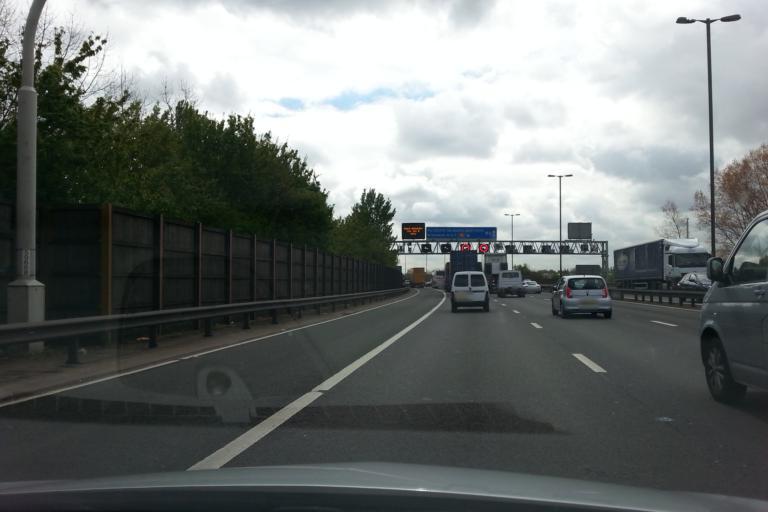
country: GB
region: England
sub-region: Walsall
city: Darlaston
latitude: 52.5720
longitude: -2.0120
